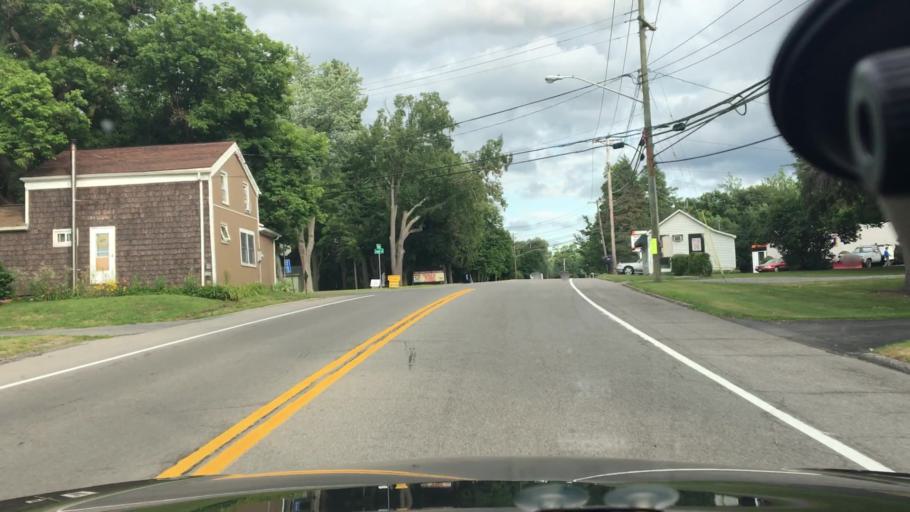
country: US
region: New York
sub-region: Erie County
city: Elma Center
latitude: 42.8174
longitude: -78.6743
